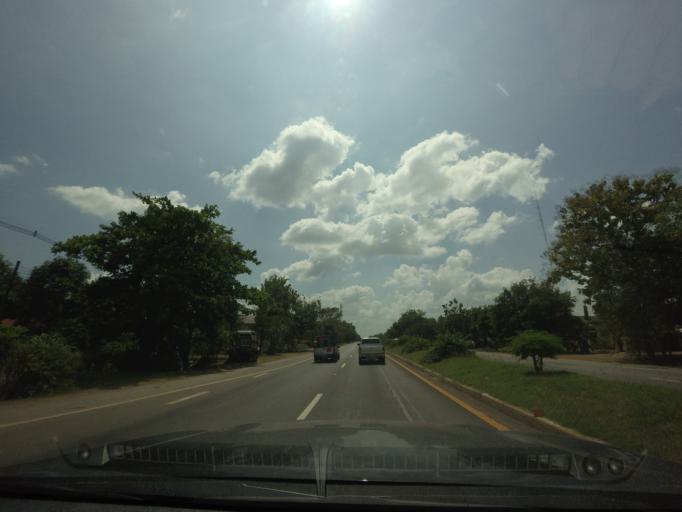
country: TH
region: Phetchabun
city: Nong Phai
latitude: 16.1388
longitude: 101.0512
